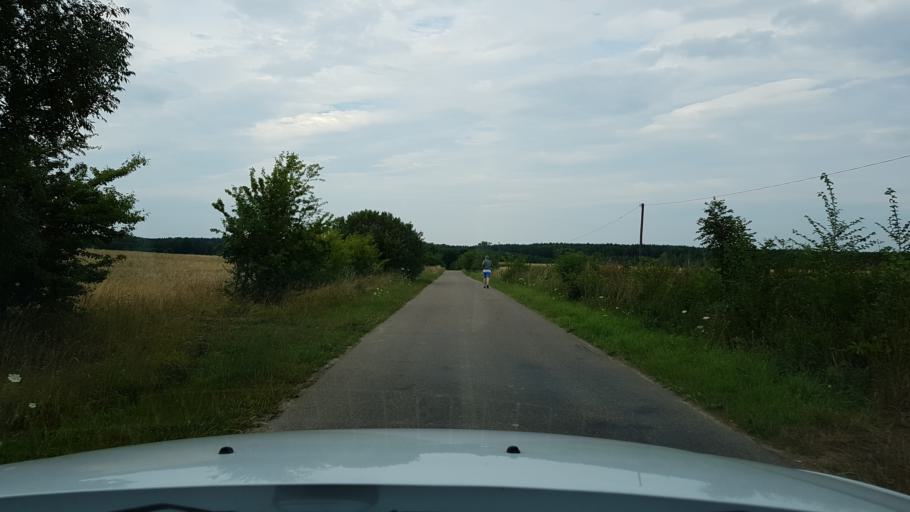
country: PL
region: West Pomeranian Voivodeship
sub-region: Powiat drawski
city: Wierzchowo
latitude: 53.4662
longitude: 16.1158
